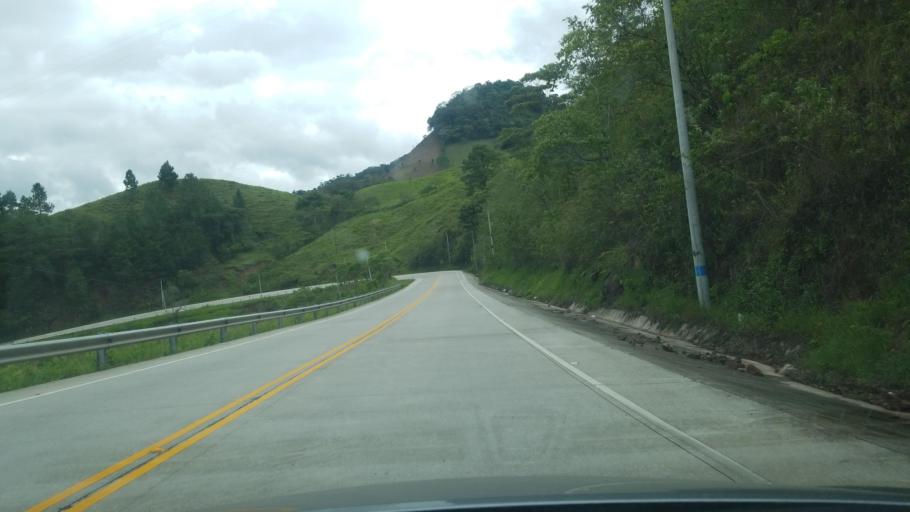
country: HN
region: Copan
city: San Jeronimo
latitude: 14.9308
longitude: -88.9505
